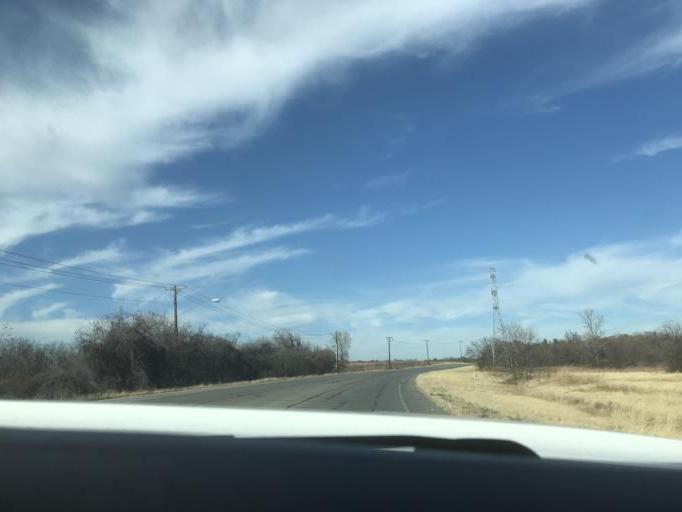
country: US
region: Texas
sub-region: Erath County
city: Stephenville
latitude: 32.2070
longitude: -98.2478
